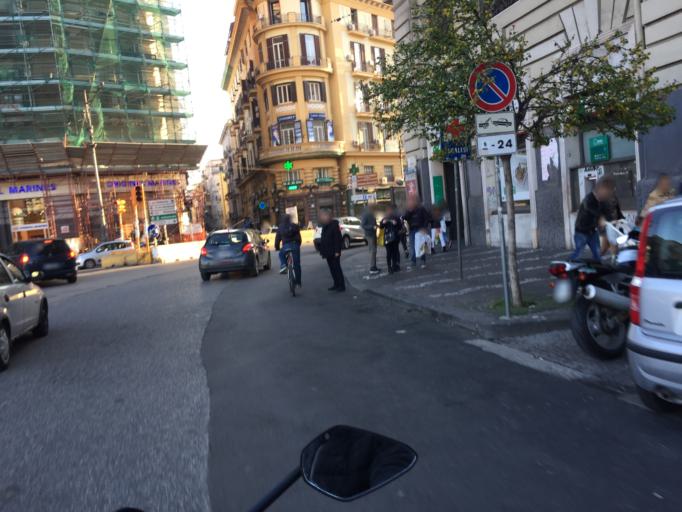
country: IT
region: Campania
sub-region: Provincia di Napoli
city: Napoli
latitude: 40.8518
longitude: 14.2676
